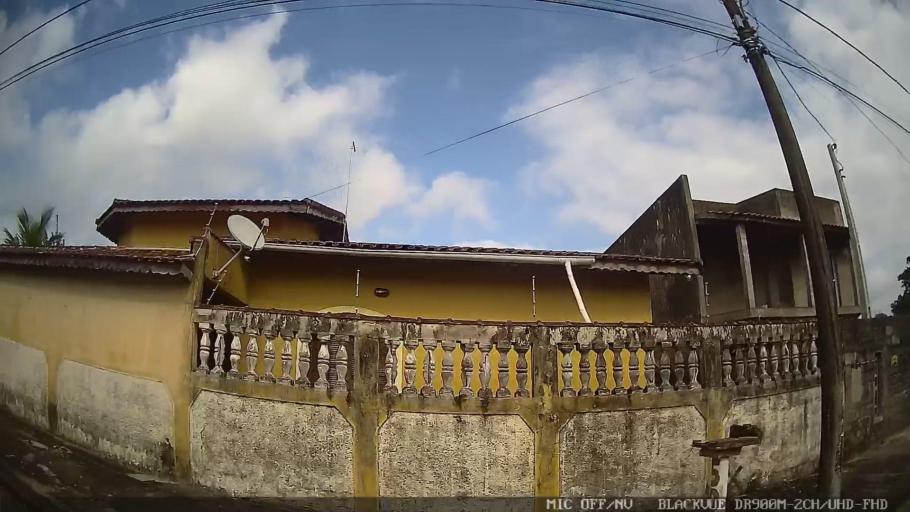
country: BR
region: Sao Paulo
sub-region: Itanhaem
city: Itanhaem
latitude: -24.2004
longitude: -46.8266
